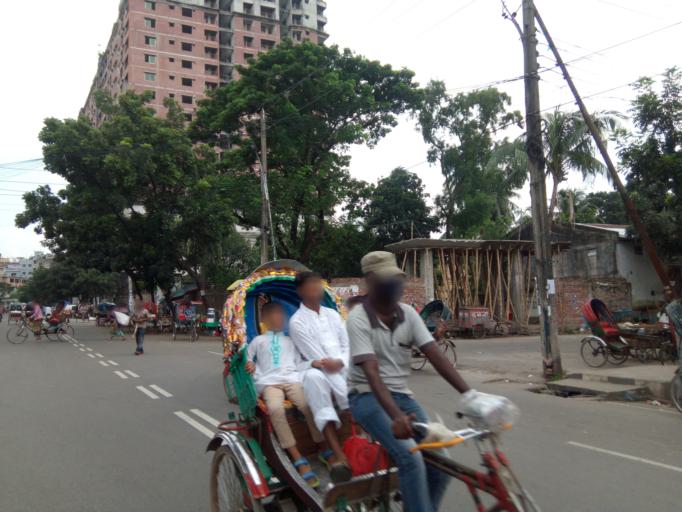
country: BD
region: Dhaka
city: Azimpur
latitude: 23.7231
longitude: 90.3875
